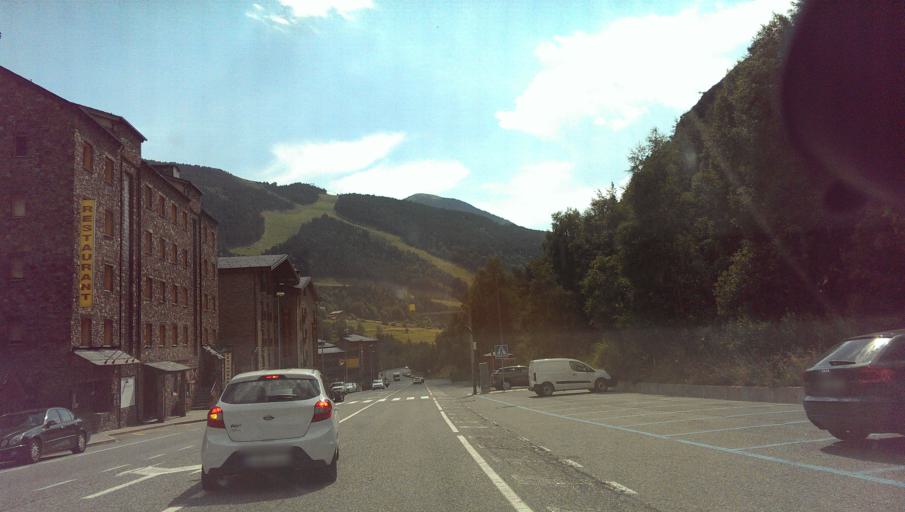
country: AD
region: Canillo
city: El Tarter
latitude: 42.5801
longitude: 1.6598
